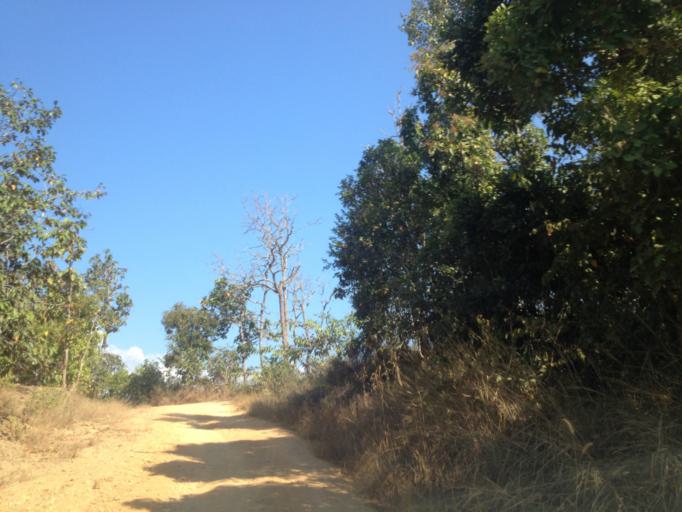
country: TH
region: Mae Hong Son
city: Ban Huai I Huak
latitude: 18.1169
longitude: 98.2079
